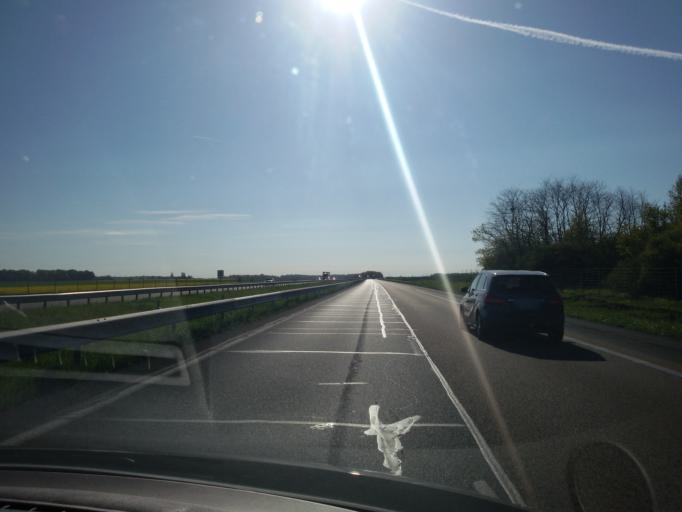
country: FR
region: Ile-de-France
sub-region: Departement de Seine-et-Marne
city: Egreville
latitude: 48.1328
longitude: 2.9378
